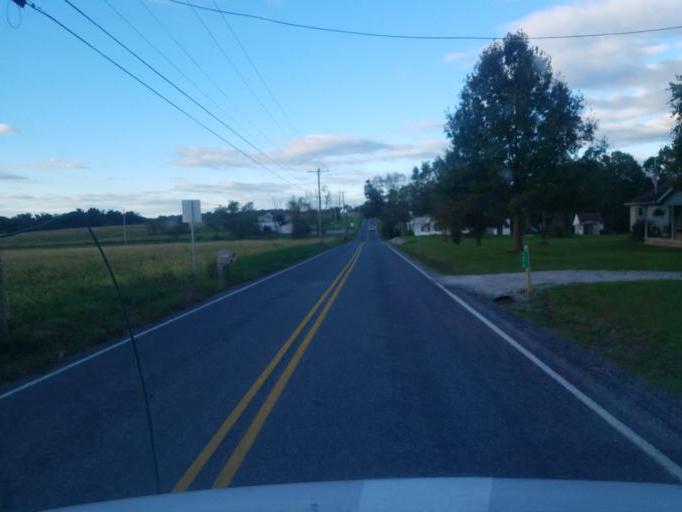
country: US
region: Pennsylvania
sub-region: Adams County
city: Lake Meade
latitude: 39.9274
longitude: -77.0616
